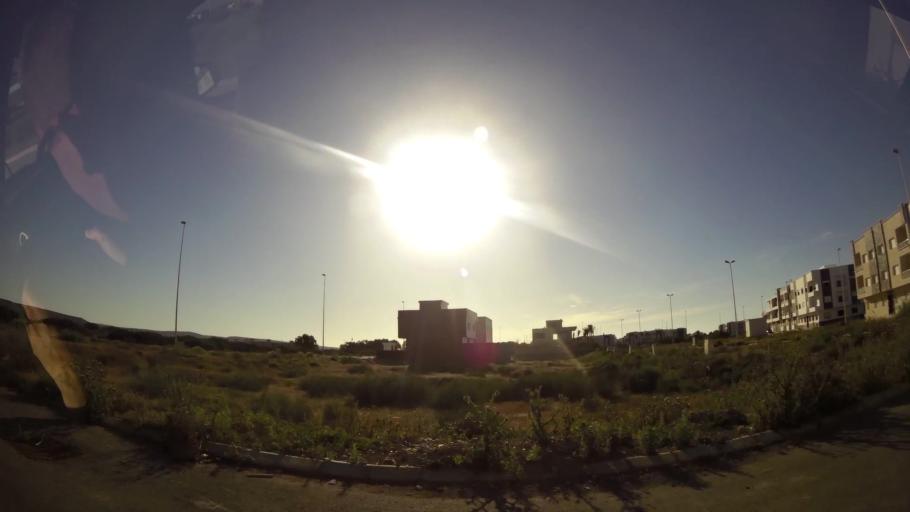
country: MA
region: Oriental
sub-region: Berkane-Taourirt
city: Madagh
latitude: 35.0909
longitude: -2.2592
